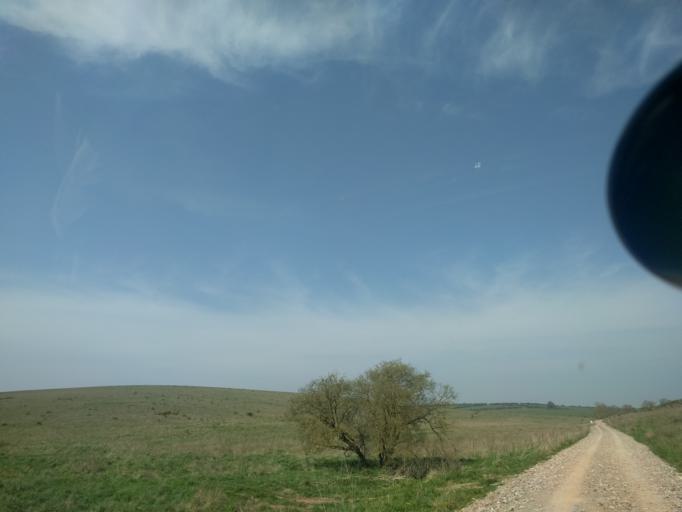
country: GB
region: England
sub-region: Wiltshire
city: Edington
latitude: 51.2403
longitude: -2.0956
